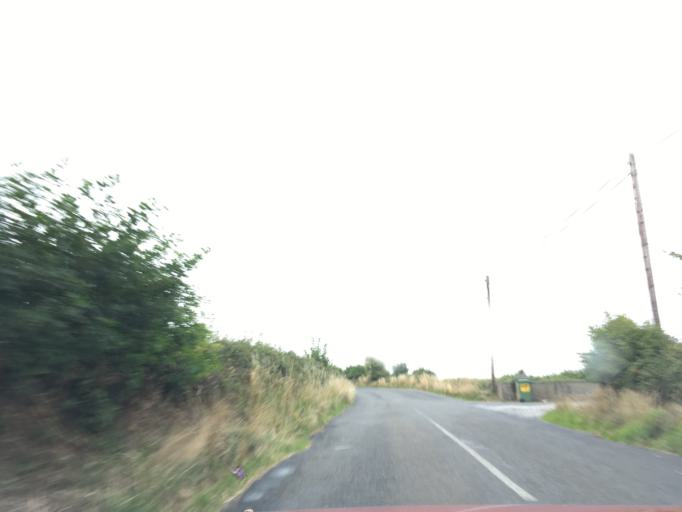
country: IE
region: Munster
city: Cashel
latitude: 52.4681
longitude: -7.8436
